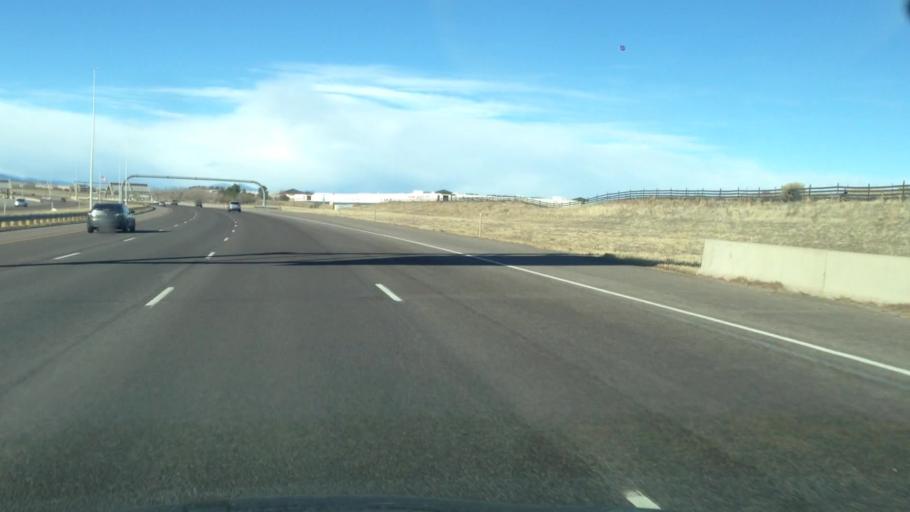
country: US
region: Colorado
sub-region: Arapahoe County
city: Dove Valley
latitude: 39.5559
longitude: -104.8149
